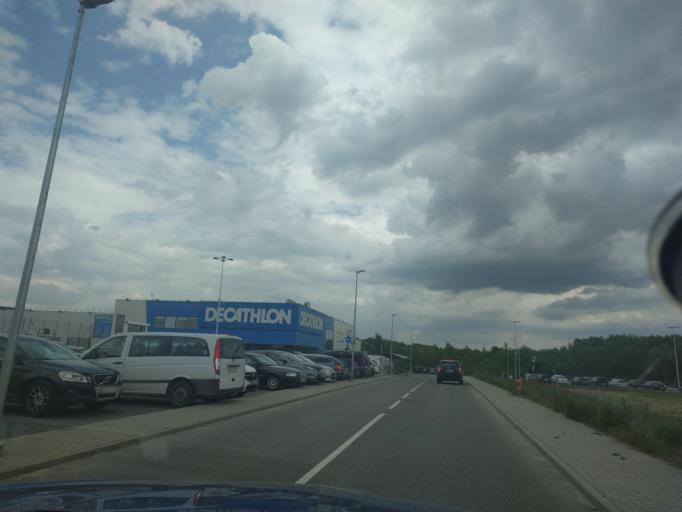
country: LT
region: Vilnius County
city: Naujamiestis
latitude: 54.6492
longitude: 25.2789
